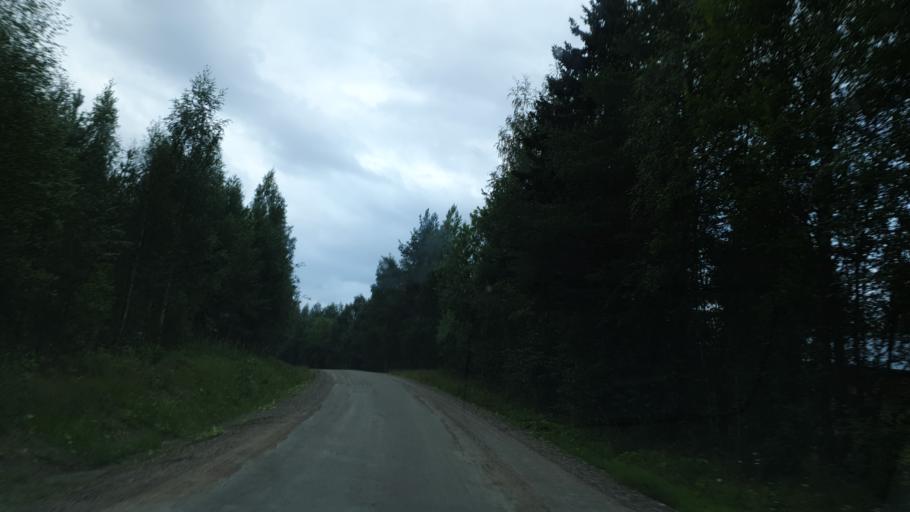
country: FI
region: Kainuu
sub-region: Kehys-Kainuu
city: Kuhmo
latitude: 64.1974
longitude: 29.3664
